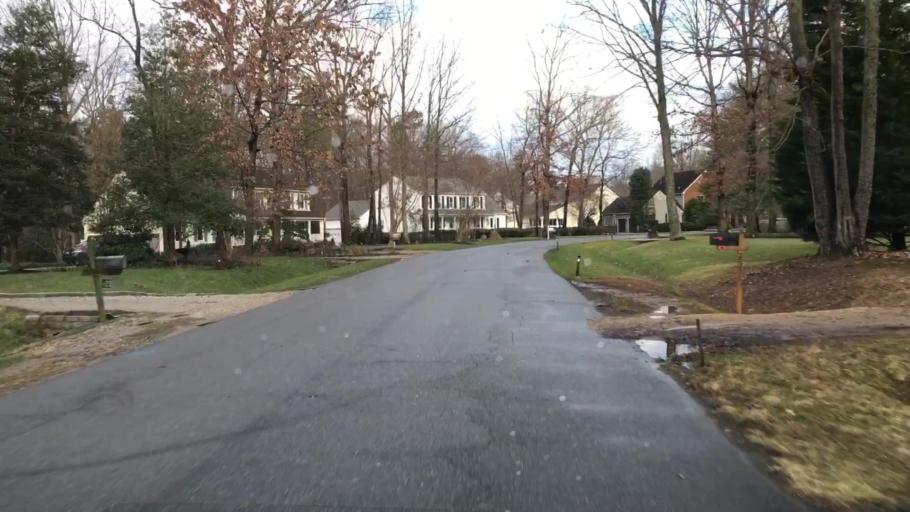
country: US
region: Virginia
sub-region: Chesterfield County
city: Bon Air
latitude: 37.5280
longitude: -77.6034
